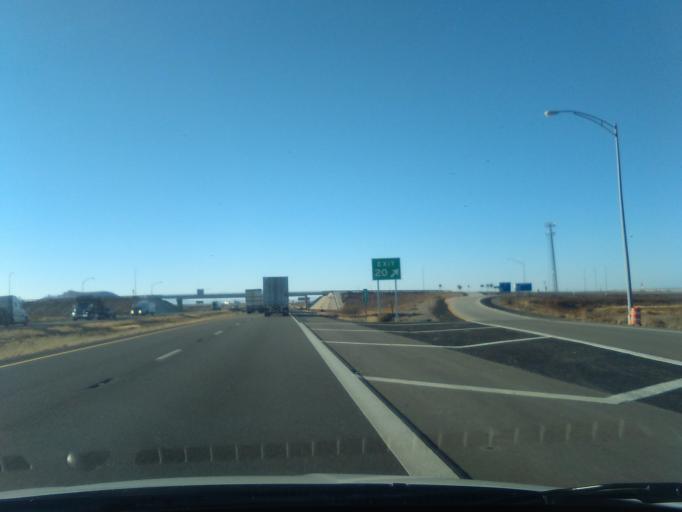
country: US
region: New Mexico
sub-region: Hidalgo County
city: Lordsburg
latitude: 32.3518
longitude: -108.7377
